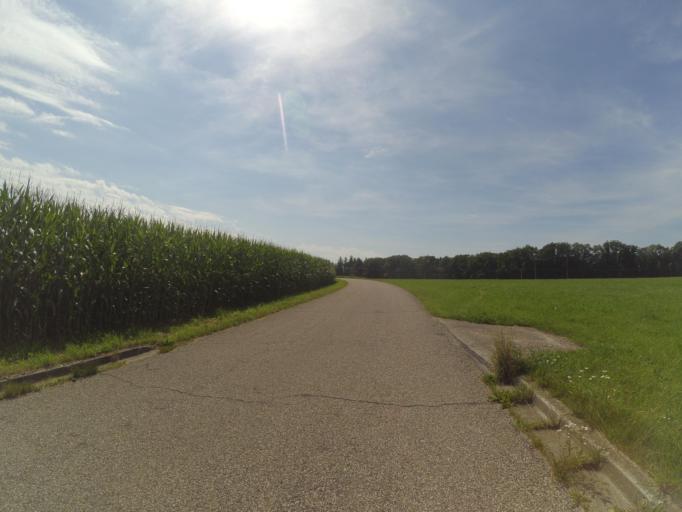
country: DE
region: Bavaria
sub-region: Swabia
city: Unteregg
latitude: 47.9640
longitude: 10.4548
